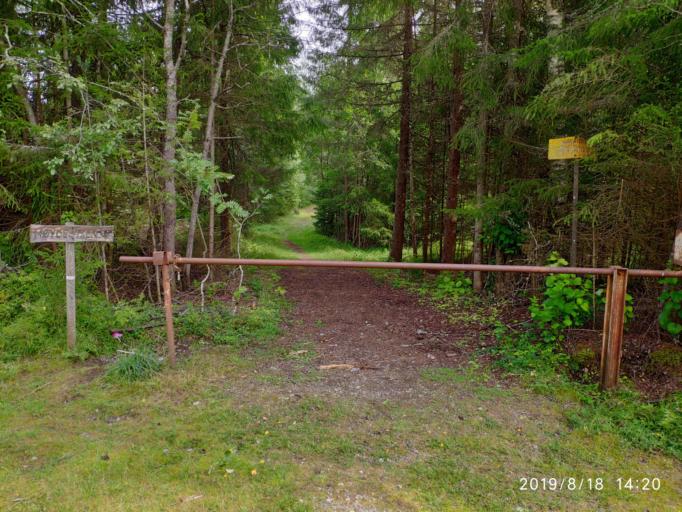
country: NO
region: Akershus
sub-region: Ullensaker
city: Jessheim
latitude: 60.1945
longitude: 11.2116
